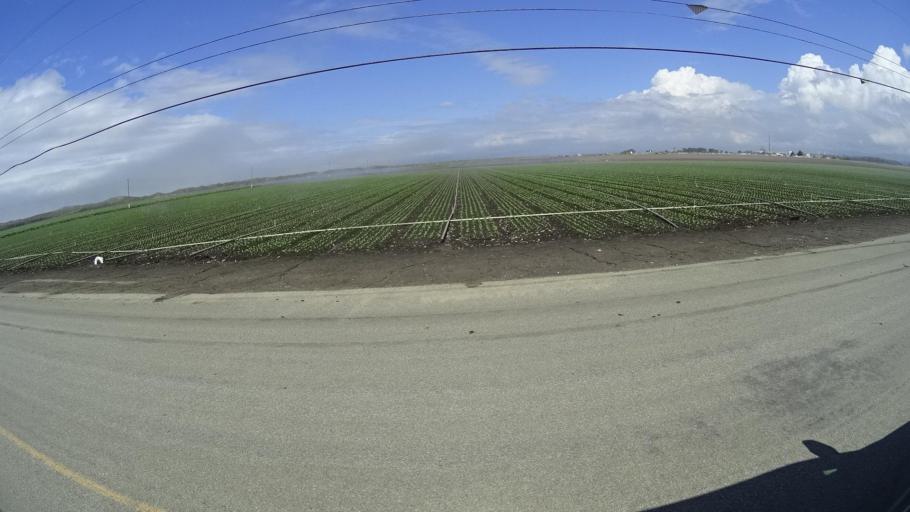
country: US
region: California
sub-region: Monterey County
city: Castroville
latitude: 36.7748
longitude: -121.7850
